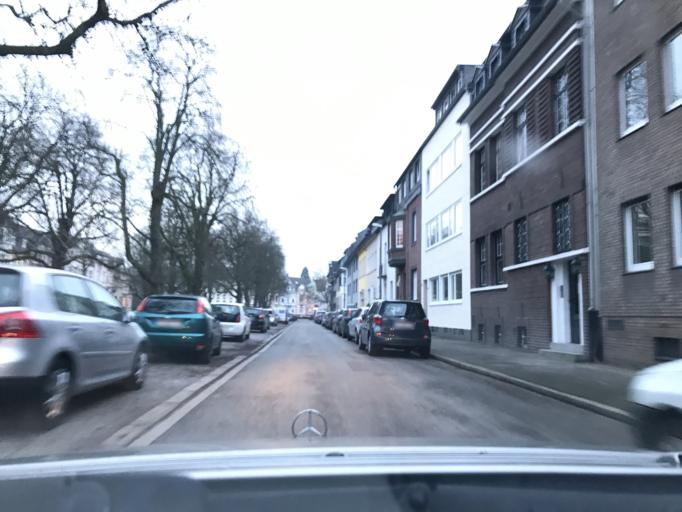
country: DE
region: North Rhine-Westphalia
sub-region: Regierungsbezirk Dusseldorf
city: Krefeld
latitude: 51.3423
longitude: 6.5761
